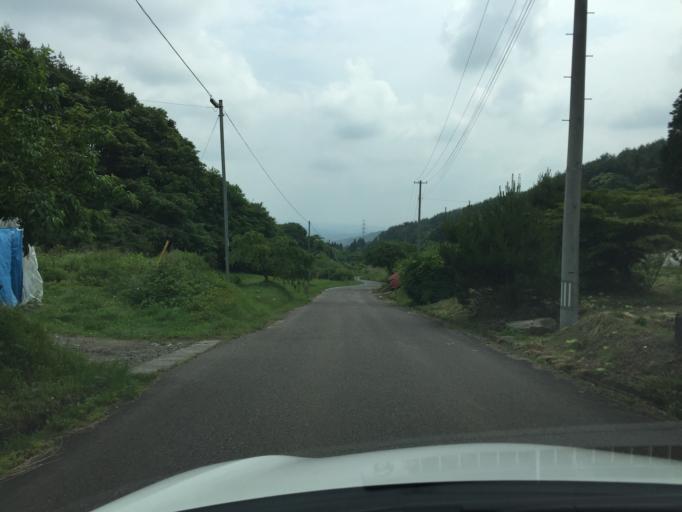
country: JP
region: Fukushima
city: Ishikawa
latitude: 37.2570
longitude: 140.4986
